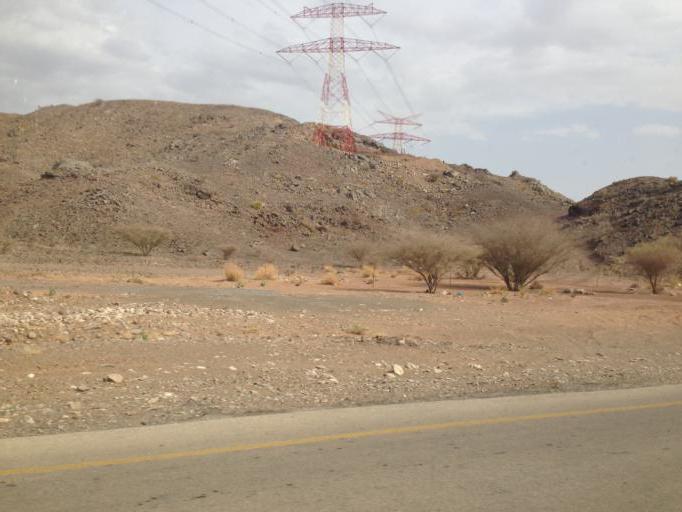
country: OM
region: Ash Sharqiyah
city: Badiyah
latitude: 22.5234
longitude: 58.9505
